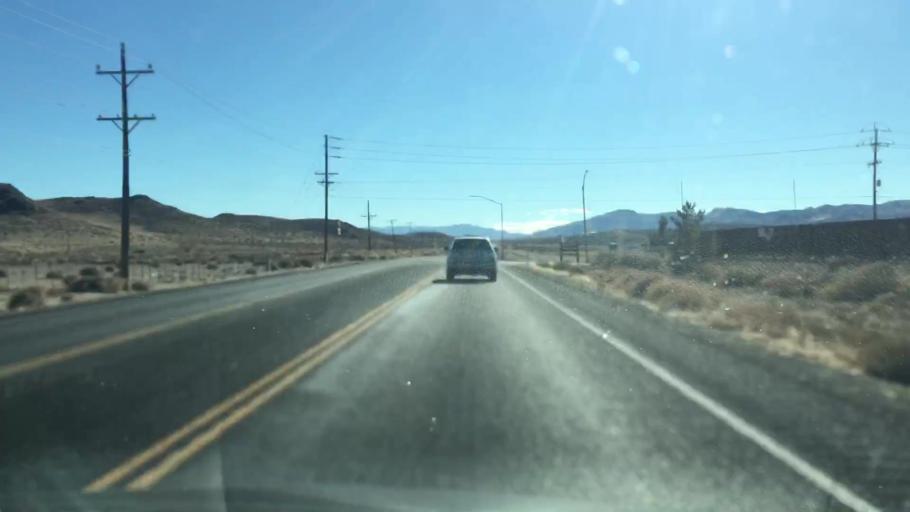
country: US
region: Nevada
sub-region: Lyon County
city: Yerington
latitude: 39.0270
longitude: -119.1816
